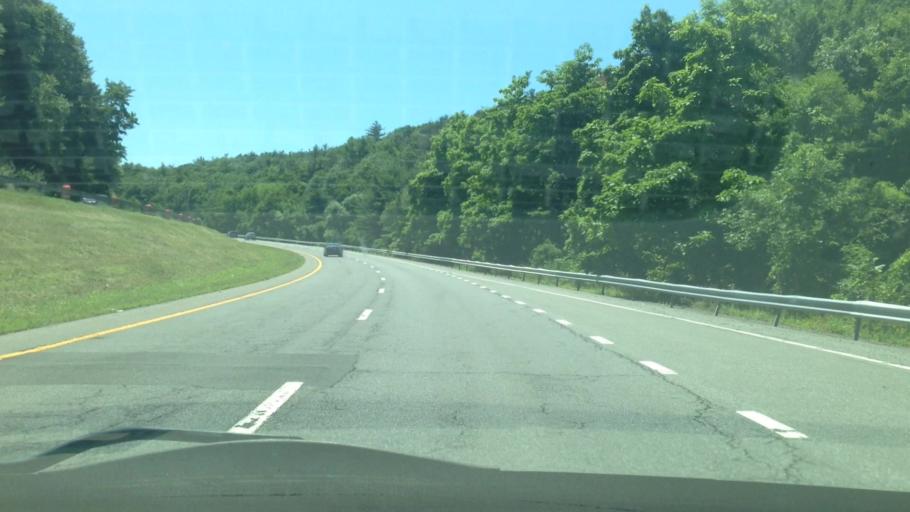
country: US
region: New York
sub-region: Ulster County
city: Lake Katrine
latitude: 41.9740
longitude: -74.0194
